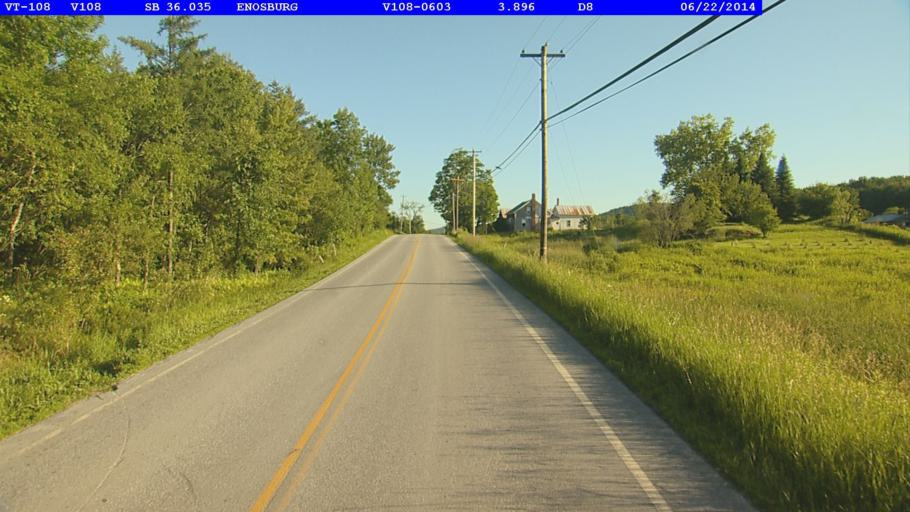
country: US
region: Vermont
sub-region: Franklin County
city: Enosburg Falls
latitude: 44.8917
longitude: -72.8020
